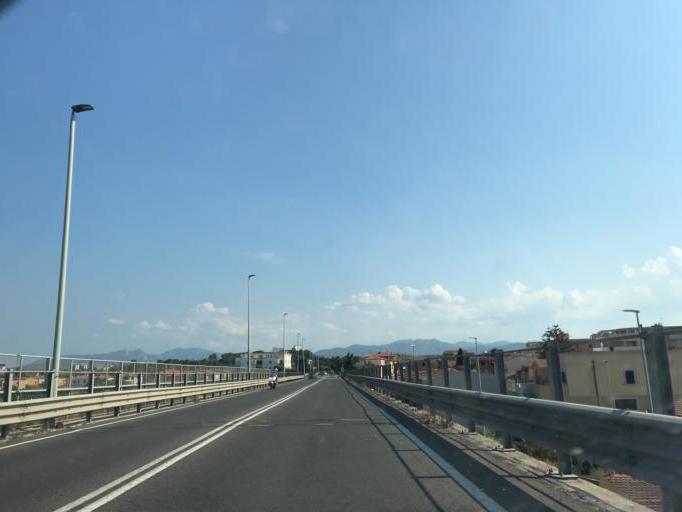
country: IT
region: Sardinia
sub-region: Provincia di Olbia-Tempio
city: Olbia
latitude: 40.9174
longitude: 9.5015
